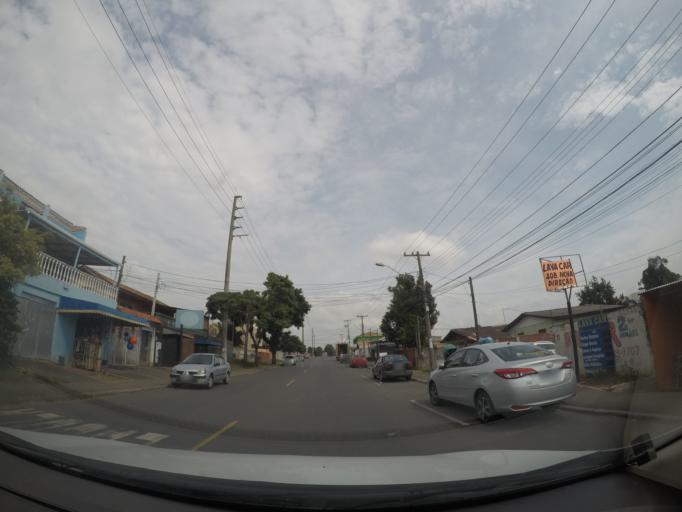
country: BR
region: Parana
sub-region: Sao Jose Dos Pinhais
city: Sao Jose dos Pinhais
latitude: -25.5246
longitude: -49.2867
